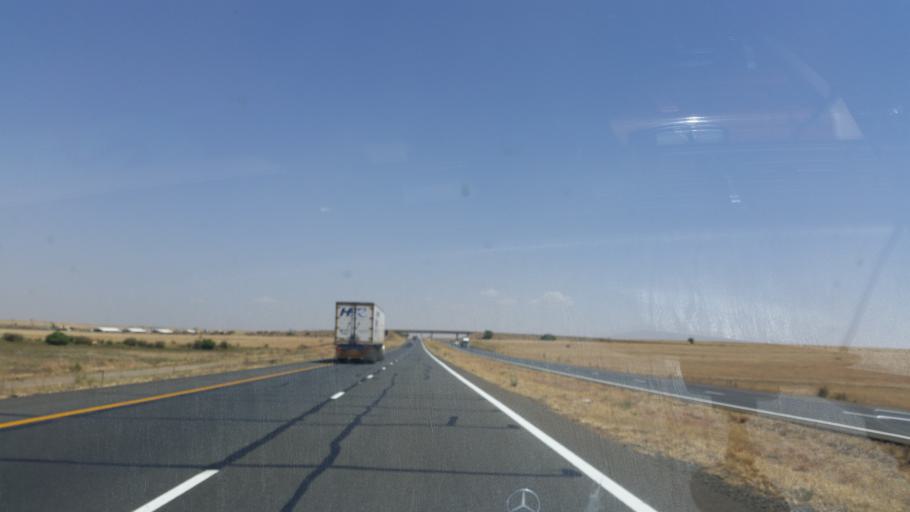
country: ZA
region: Orange Free State
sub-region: Lejweleputswa District Municipality
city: Brandfort
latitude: -28.8643
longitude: 26.5371
